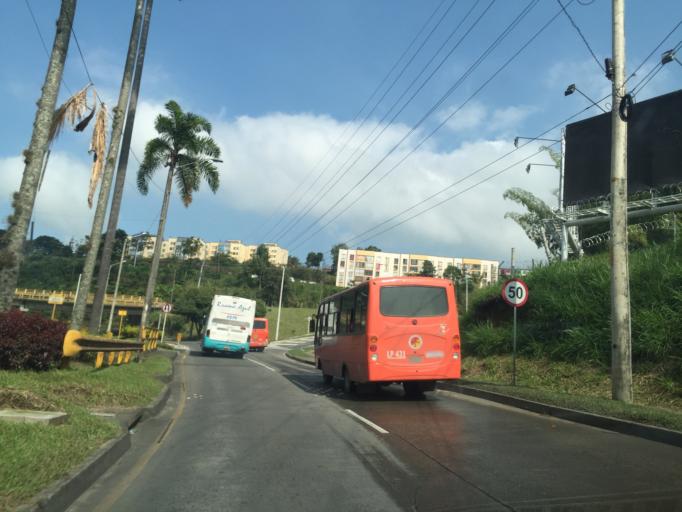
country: CO
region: Risaralda
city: Pereira
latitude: 4.8091
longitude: -75.7329
